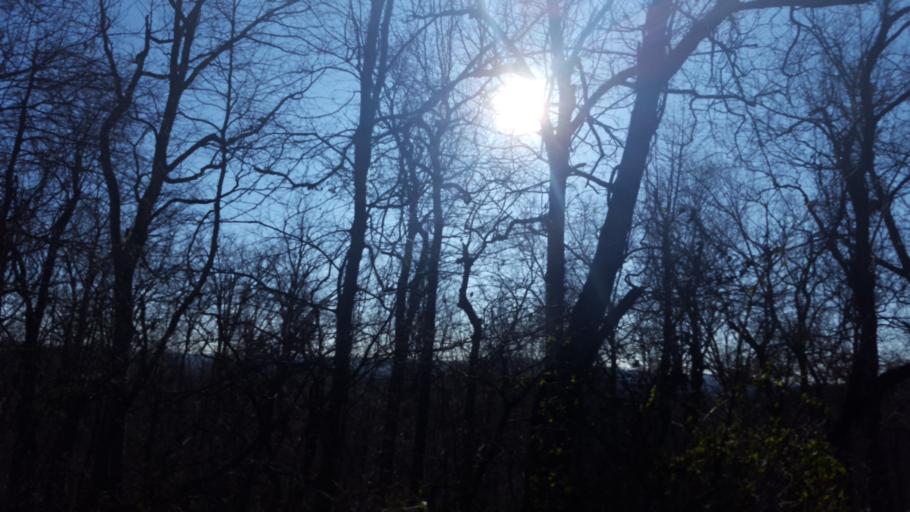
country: US
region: Kentucky
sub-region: Crittenden County
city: Marion
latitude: 37.4488
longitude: -88.0863
